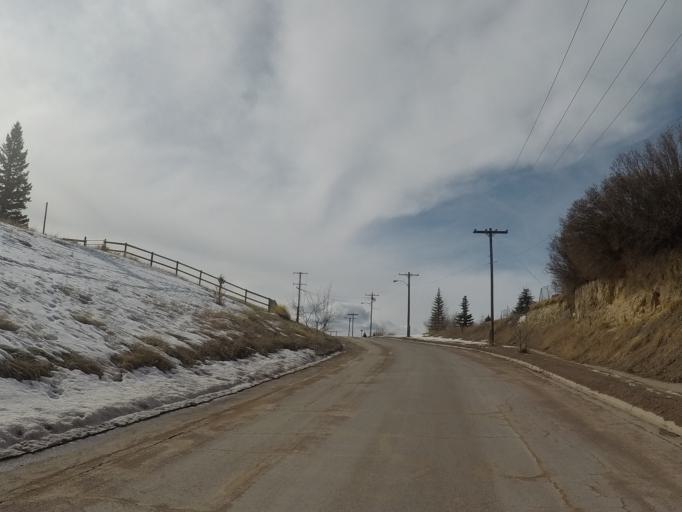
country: US
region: Montana
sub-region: Granite County
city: Philipsburg
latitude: 46.3308
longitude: -113.2934
